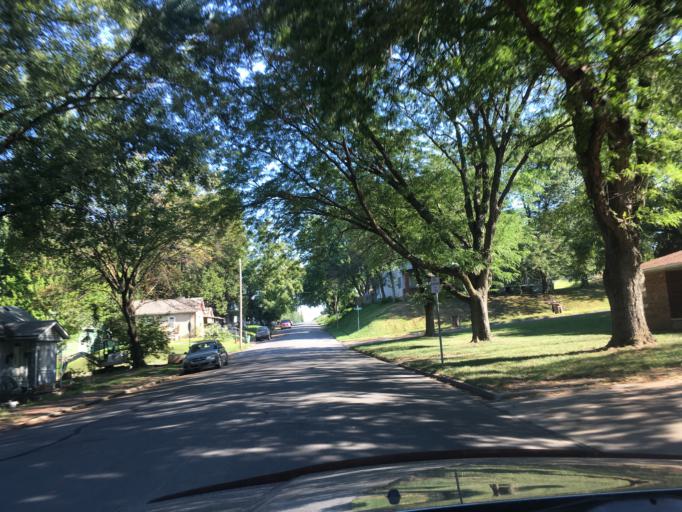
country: US
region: Kansas
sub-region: Atchison County
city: Atchison
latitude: 39.5701
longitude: -95.1203
